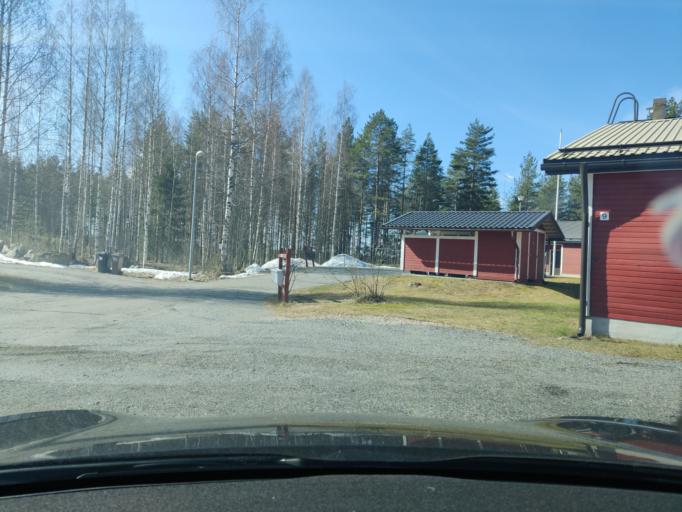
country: FI
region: Northern Savo
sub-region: Kuopio
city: Vehmersalmi
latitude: 62.7579
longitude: 28.0347
